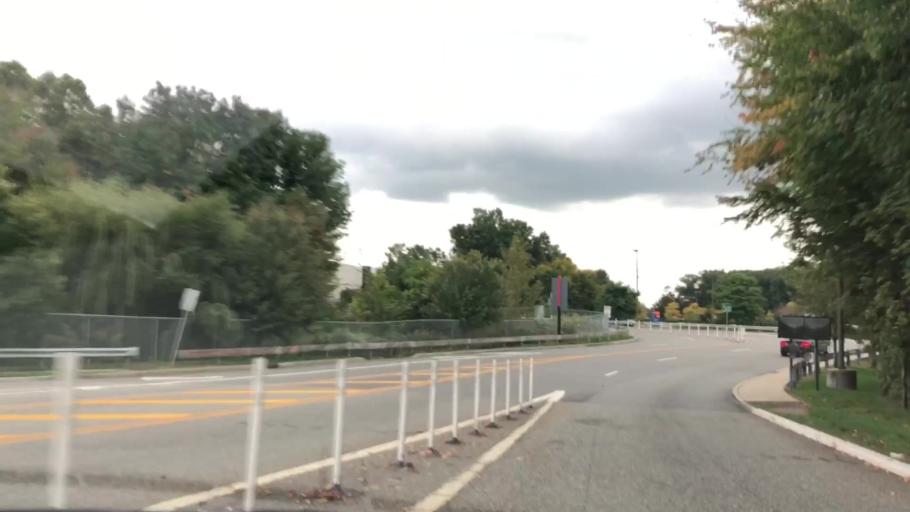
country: US
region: New Jersey
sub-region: Bergen County
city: Rochelle Park
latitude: 40.9211
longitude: -74.0783
